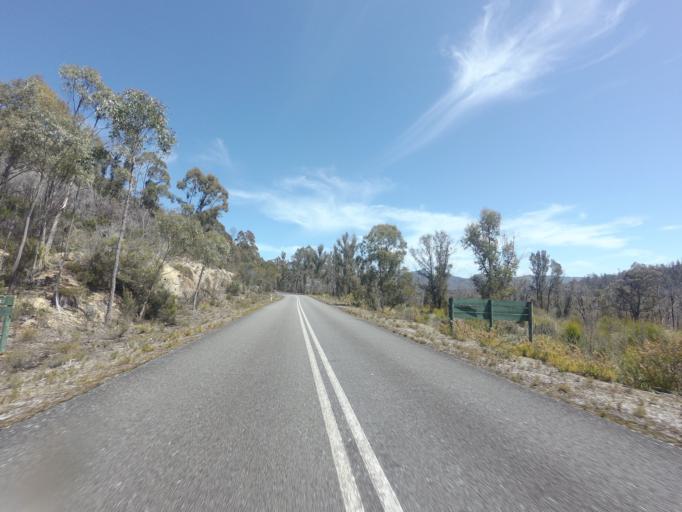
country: AU
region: Tasmania
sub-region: Huon Valley
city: Geeveston
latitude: -42.8447
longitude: 146.2486
